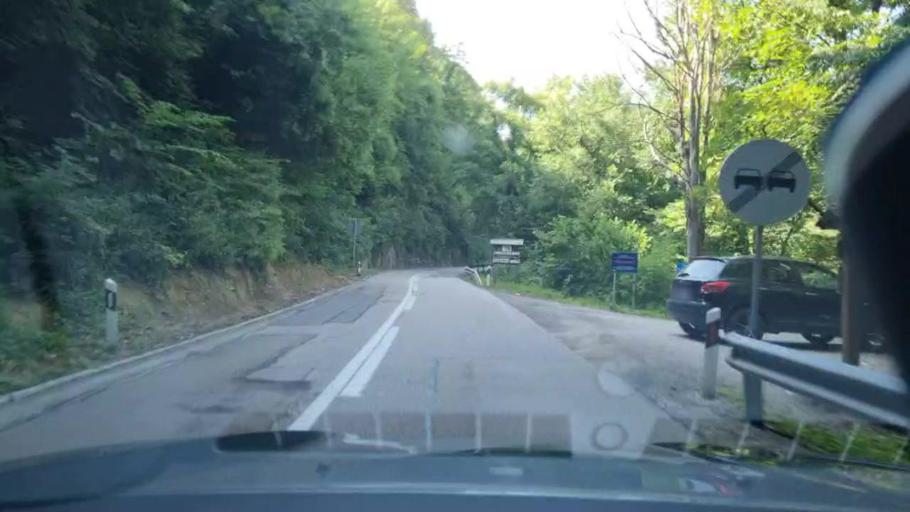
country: BA
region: Federation of Bosnia and Herzegovina
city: Bosanska Krupa
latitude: 44.8665
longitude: 16.0893
